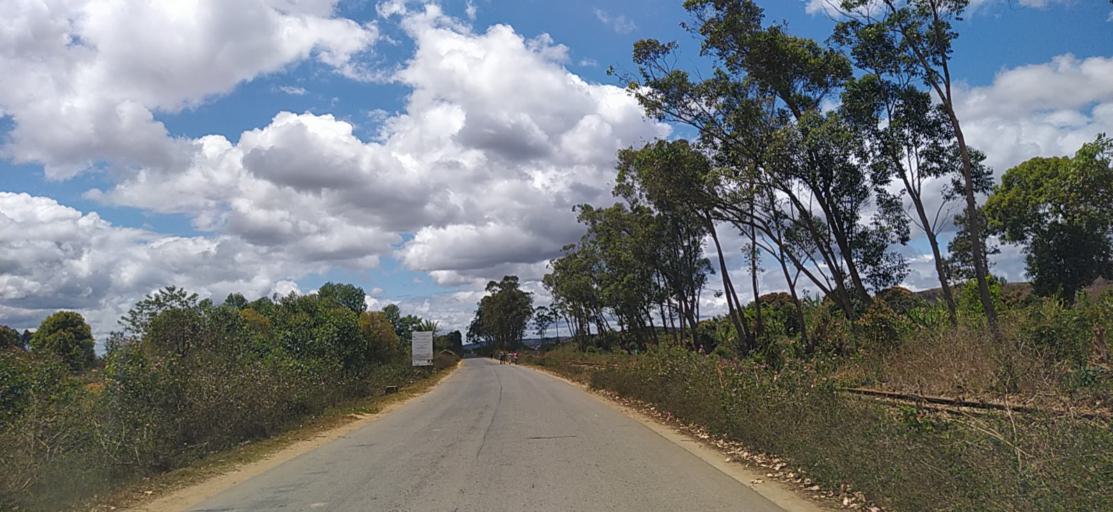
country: MG
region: Alaotra Mangoro
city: Moramanga
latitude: -18.7792
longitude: 48.2486
